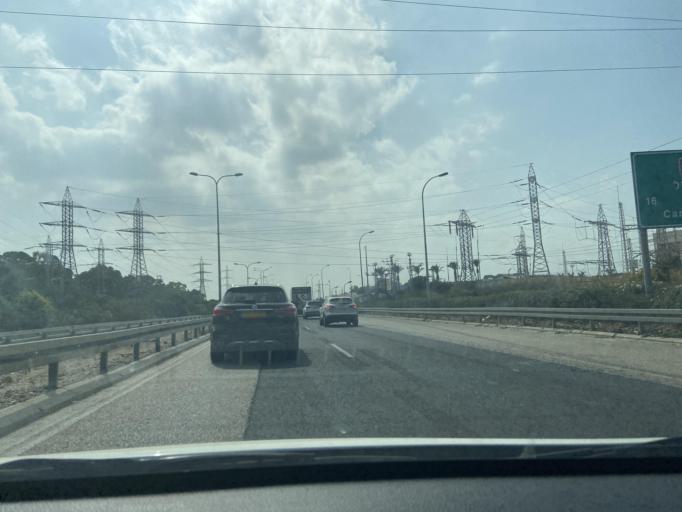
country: IL
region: Northern District
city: `Akko
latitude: 32.8956
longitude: 35.0936
